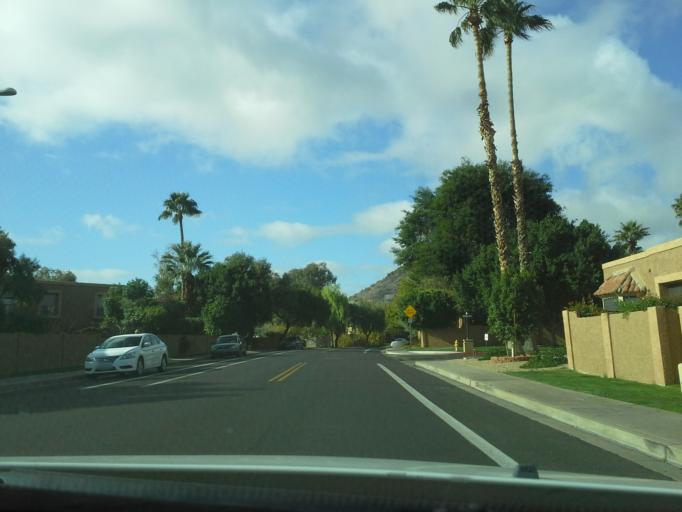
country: US
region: Arizona
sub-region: Maricopa County
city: Paradise Valley
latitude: 33.5814
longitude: -112.0607
